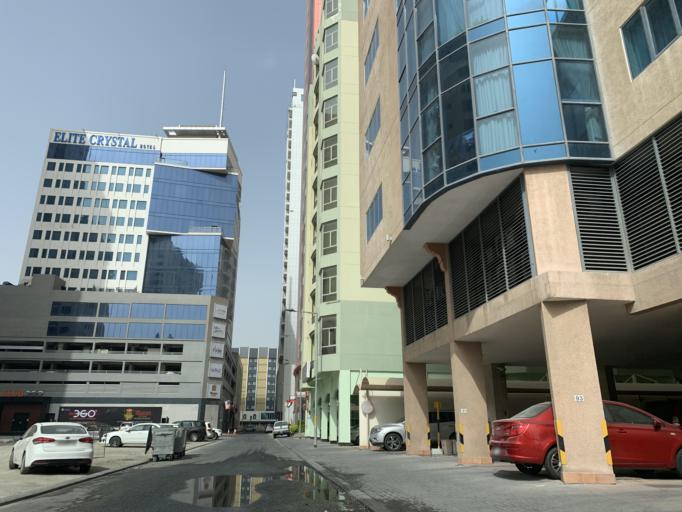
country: BH
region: Manama
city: Manama
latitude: 26.2160
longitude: 50.6122
